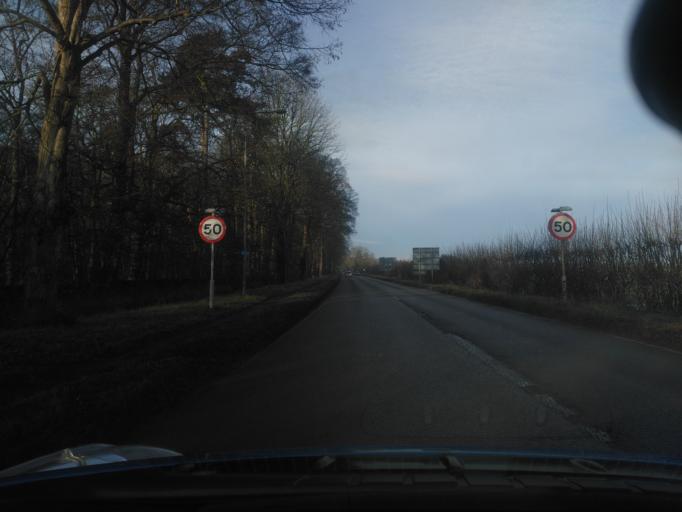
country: GB
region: England
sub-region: Oxfordshire
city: Woodstock
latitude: 51.8384
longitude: -1.3369
